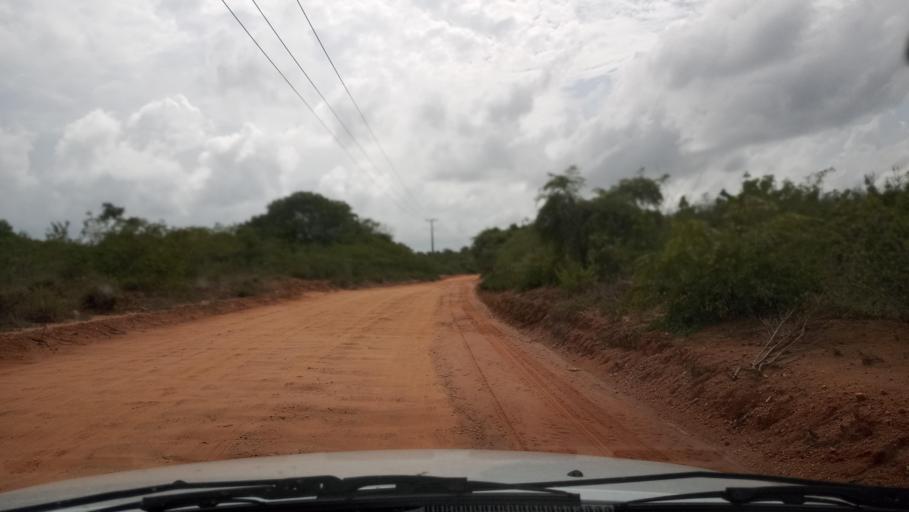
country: BR
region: Rio Grande do Norte
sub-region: Maxaranguape
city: Sao Miguel
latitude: -5.4830
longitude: -35.3196
